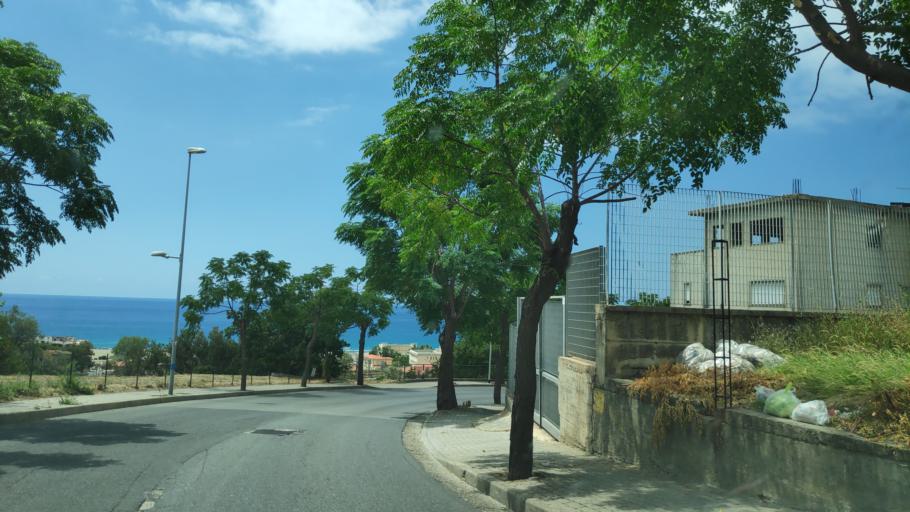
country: IT
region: Calabria
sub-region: Provincia di Cosenza
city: Paola
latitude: 39.3589
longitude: 16.0376
